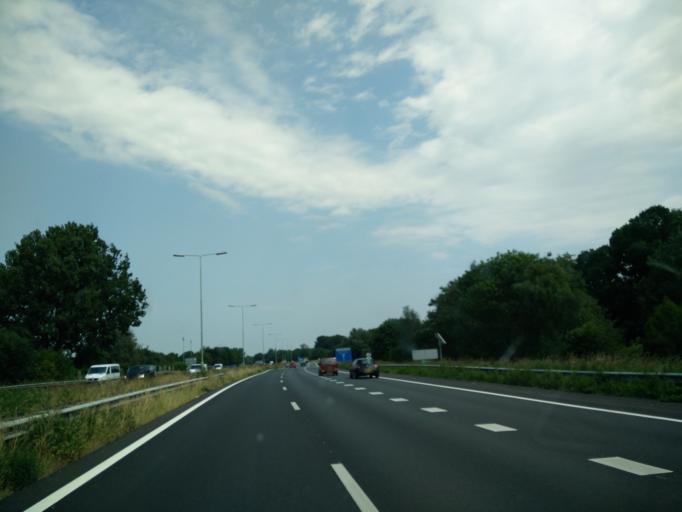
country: NL
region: South Holland
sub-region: Gemeente Dordrecht
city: Dordrecht
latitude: 51.7974
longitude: 4.6850
